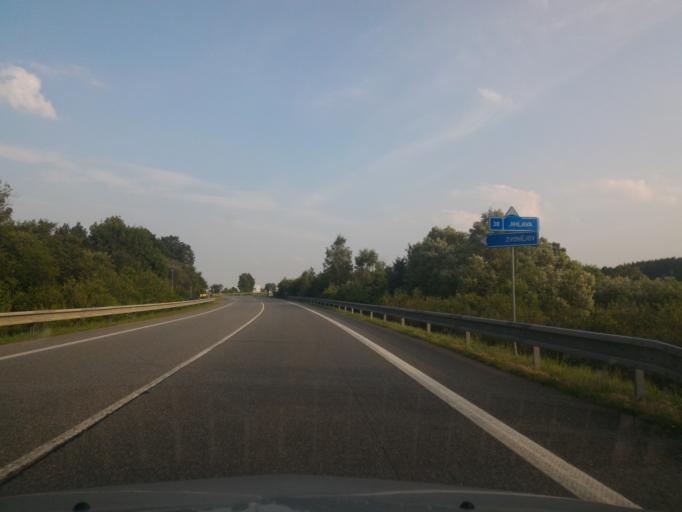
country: CZ
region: Vysocina
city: Stoky
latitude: 49.4758
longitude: 15.5932
